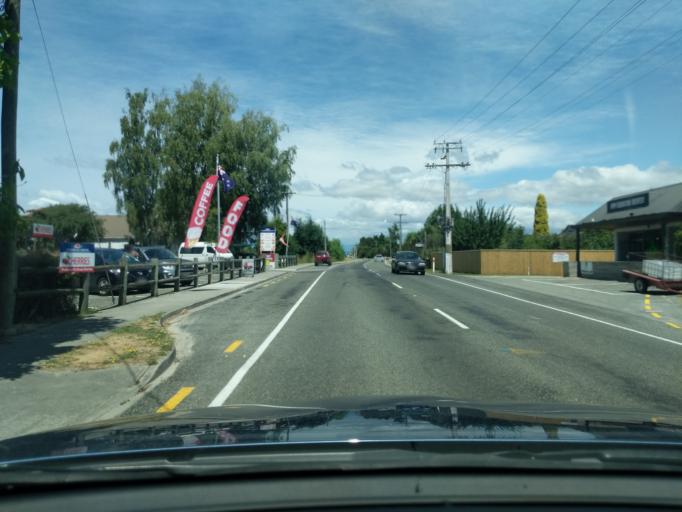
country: NZ
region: Tasman
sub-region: Tasman District
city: Motueka
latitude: -41.0797
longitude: 172.9973
